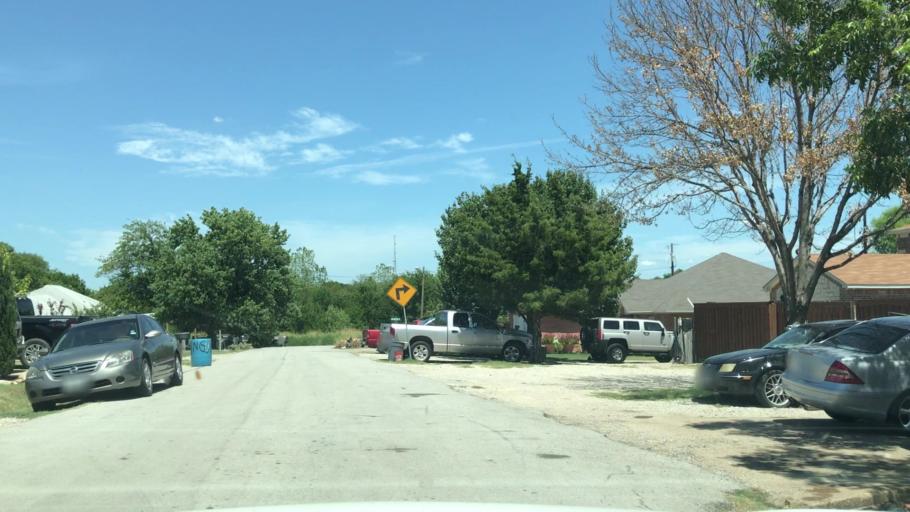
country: US
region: Texas
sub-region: Rockwall County
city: Rockwall
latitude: 32.8891
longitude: -96.4559
